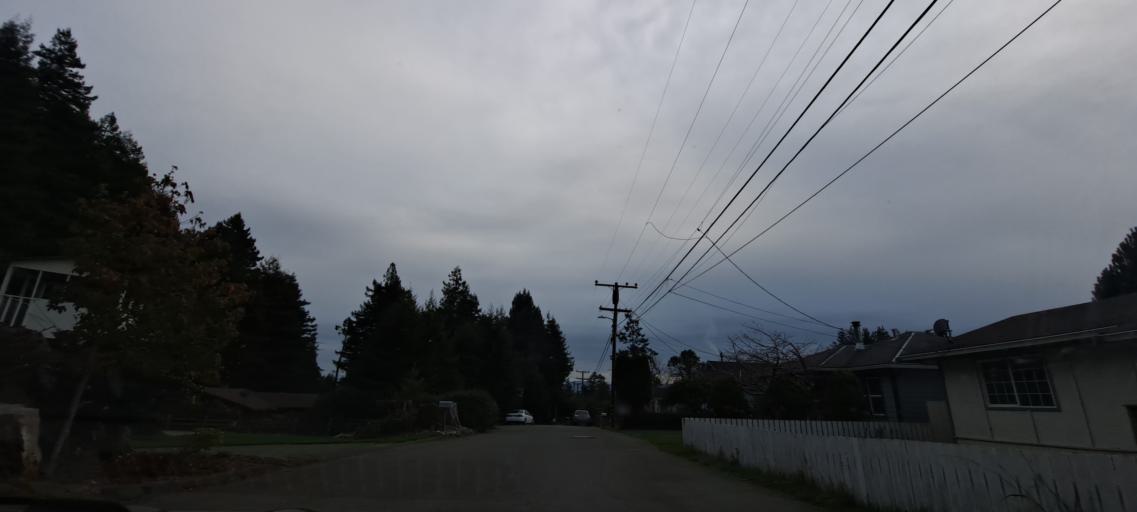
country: US
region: California
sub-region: Humboldt County
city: Fortuna
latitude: 40.6051
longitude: -124.1544
